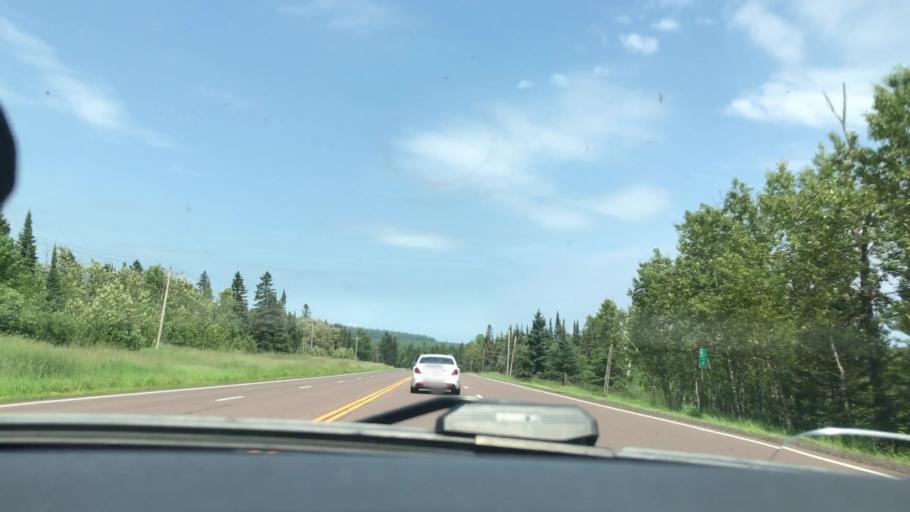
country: US
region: Minnesota
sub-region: Lake County
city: Two Harbors
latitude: 47.0819
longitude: -91.5836
